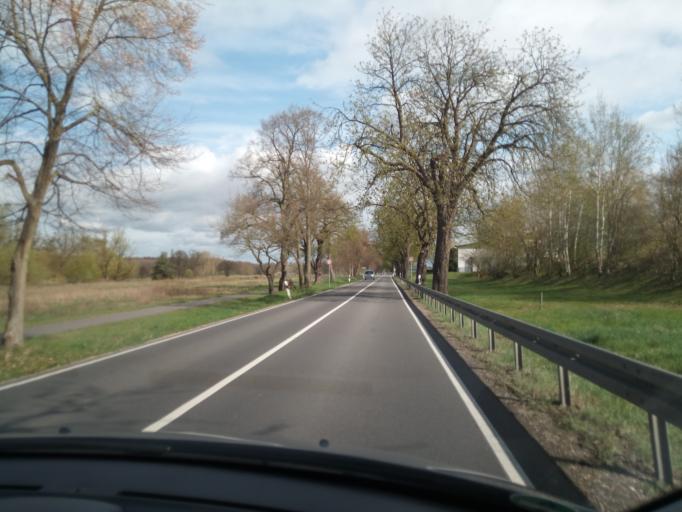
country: DE
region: Mecklenburg-Vorpommern
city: Boizenburg
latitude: 53.4139
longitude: 10.7418
